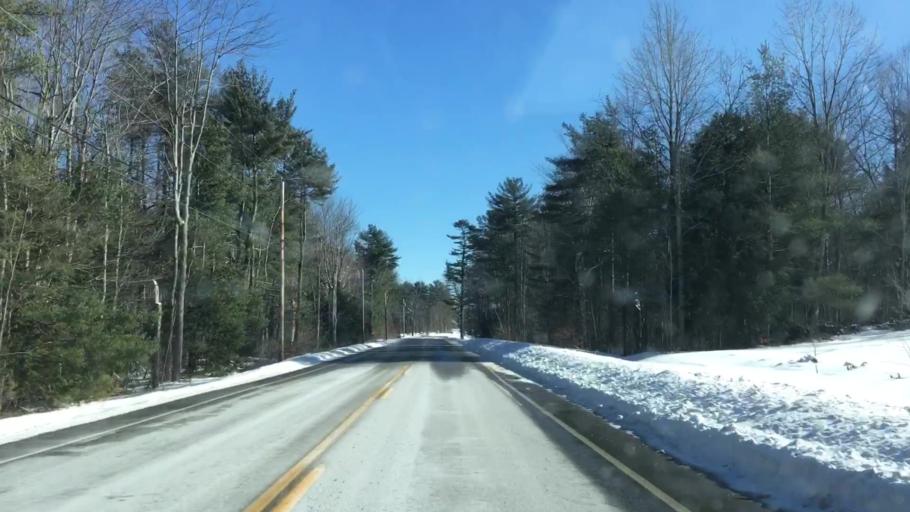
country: US
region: Maine
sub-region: Androscoggin County
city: Lisbon
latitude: 44.0265
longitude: -70.0752
